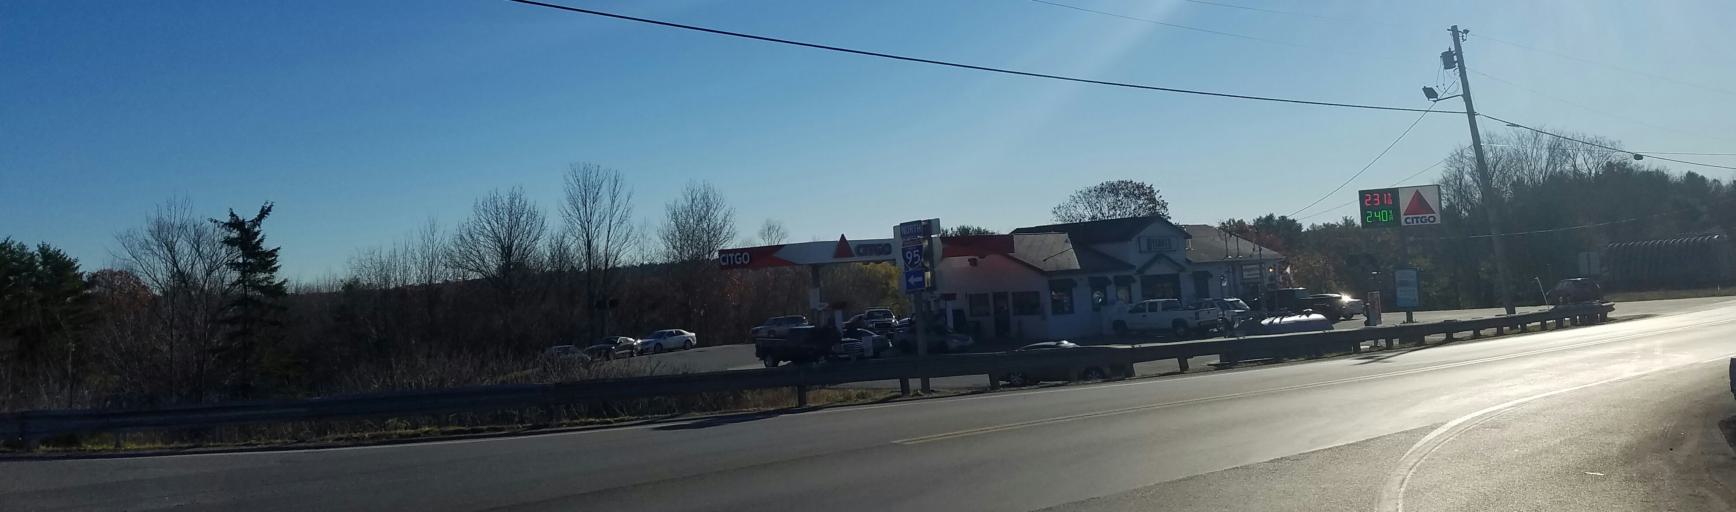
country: US
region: Maine
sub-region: Penobscot County
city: Hermon
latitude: 44.7574
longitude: -68.9741
